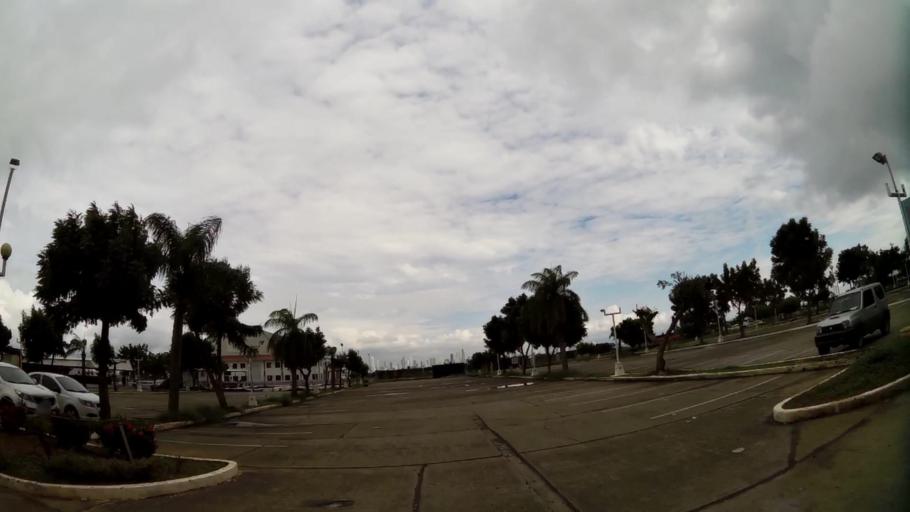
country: PA
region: Panama
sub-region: Distrito de Panama
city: Ancon
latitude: 8.9158
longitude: -79.5269
